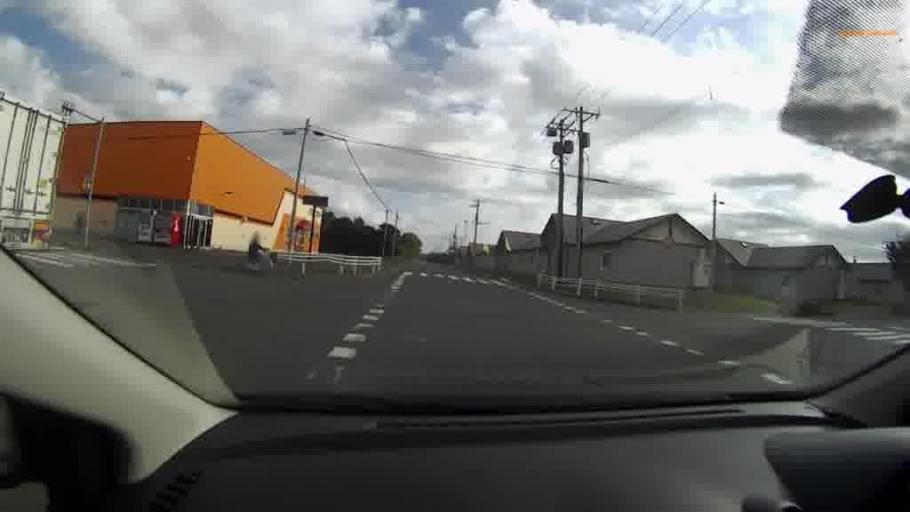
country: JP
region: Hokkaido
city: Kushiro
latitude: 42.9783
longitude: 144.1282
